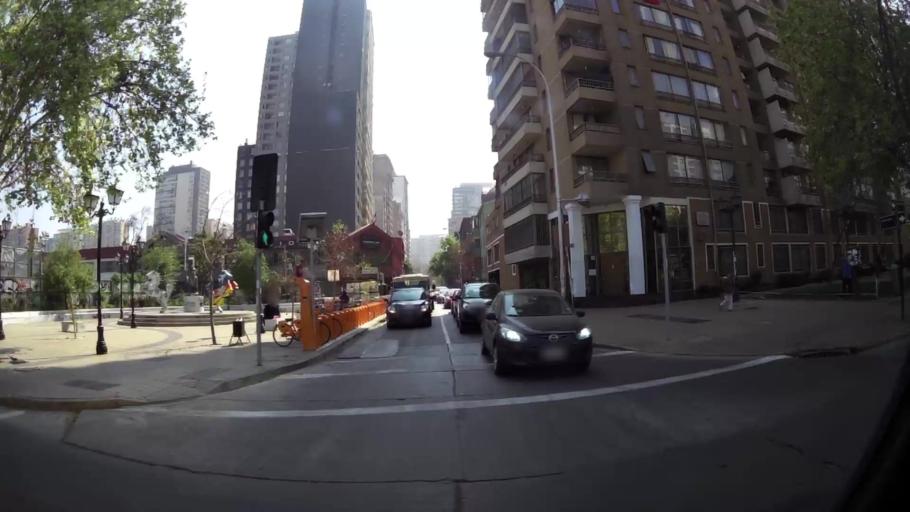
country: CL
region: Santiago Metropolitan
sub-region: Provincia de Santiago
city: Santiago
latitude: -33.4503
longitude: -70.6427
